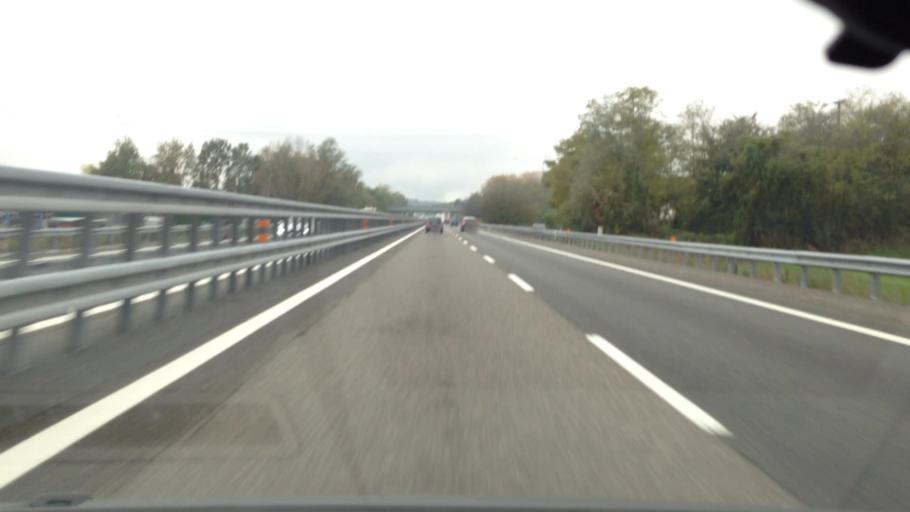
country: IT
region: Piedmont
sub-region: Provincia di Asti
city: Baldichieri d'Asti
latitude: 44.9036
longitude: 8.0865
